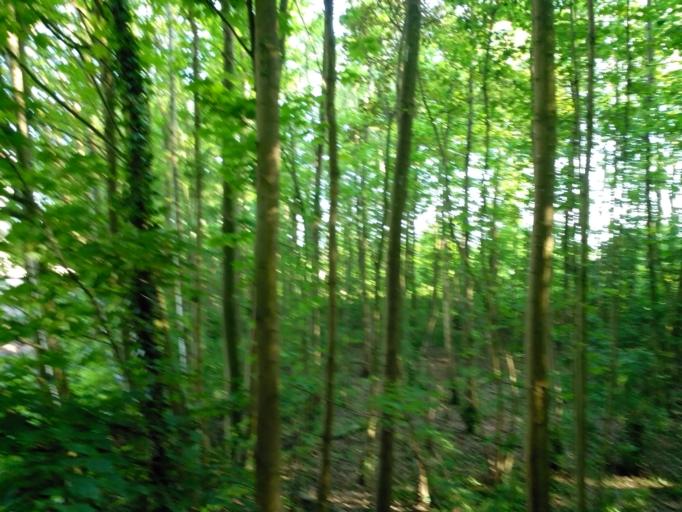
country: BE
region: Flanders
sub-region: Provincie Vlaams-Brabant
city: Bertem
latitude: 50.8752
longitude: 4.6145
